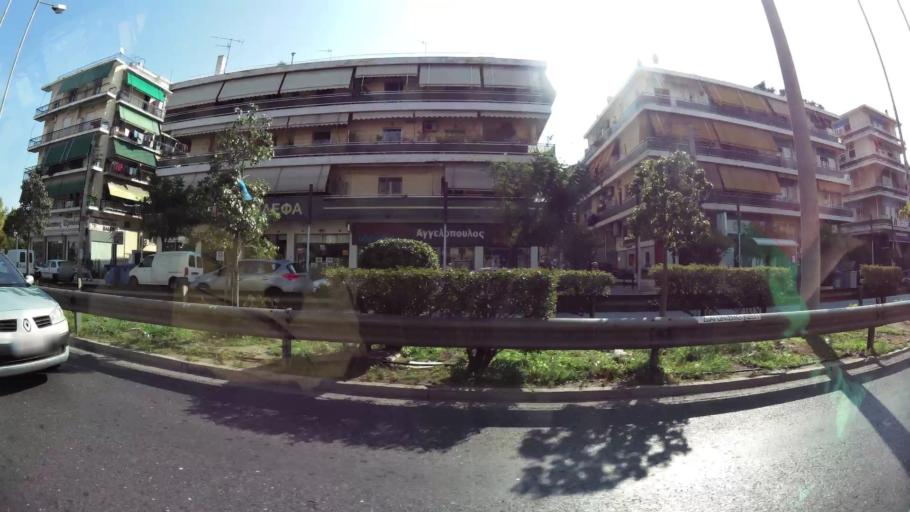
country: GR
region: Attica
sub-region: Nomarchia Athinas
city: Galatsi
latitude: 38.0199
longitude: 23.7566
